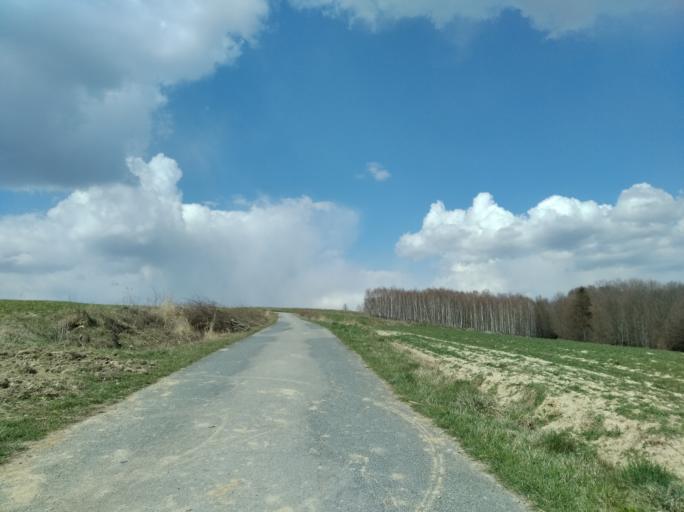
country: PL
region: Subcarpathian Voivodeship
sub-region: Powiat strzyzowski
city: Strzyzow
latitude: 49.9153
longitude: 21.7295
